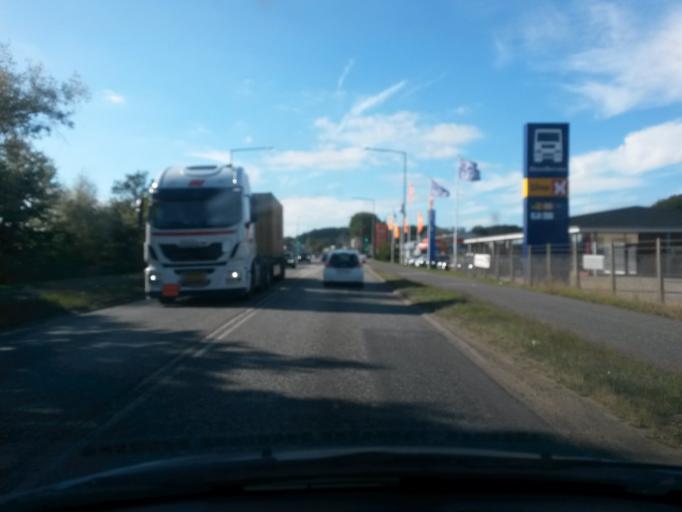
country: DK
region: Central Jutland
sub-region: Silkeborg Kommune
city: Silkeborg
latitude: 56.1865
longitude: 9.5518
